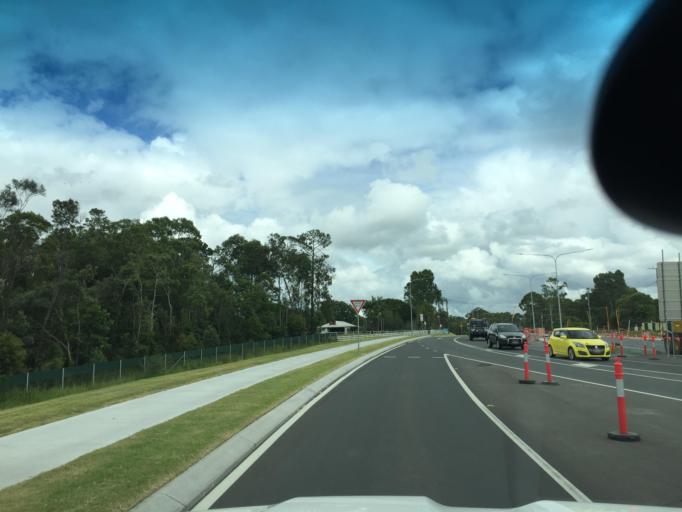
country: AU
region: Queensland
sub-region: Moreton Bay
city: Burpengary
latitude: -27.1795
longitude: 152.9801
